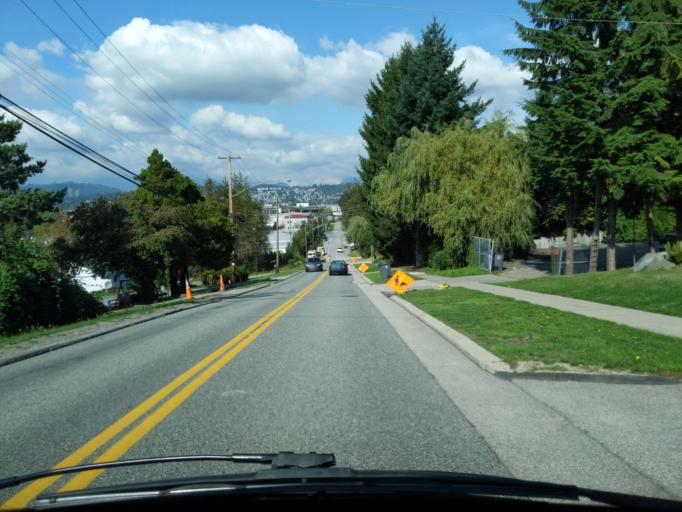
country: CA
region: British Columbia
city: New Westminster
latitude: 49.2082
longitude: -122.8563
